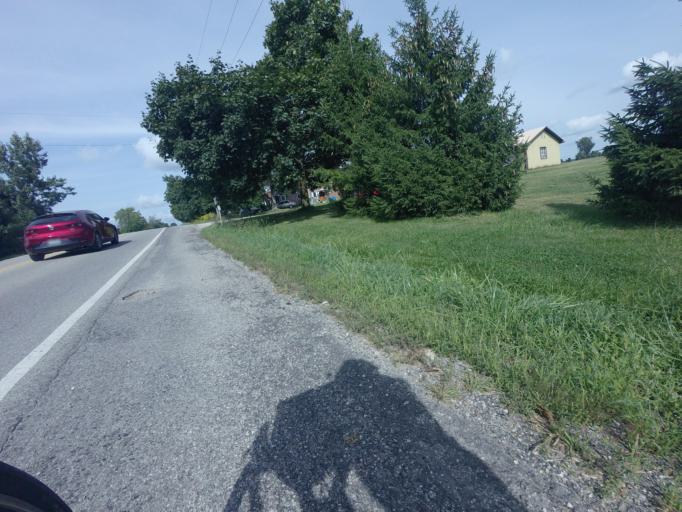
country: CA
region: Ontario
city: Waterloo
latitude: 43.5874
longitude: -80.4662
